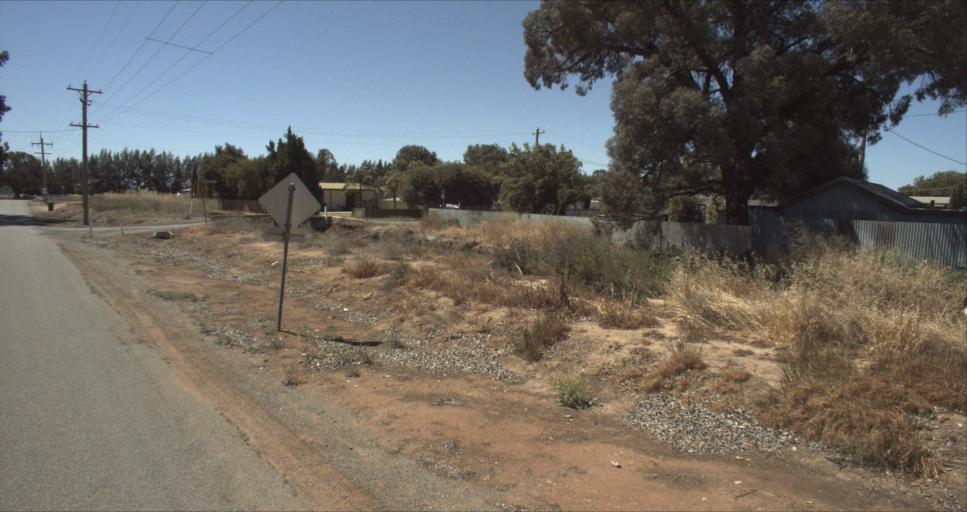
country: AU
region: New South Wales
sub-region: Leeton
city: Leeton
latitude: -34.5238
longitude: 146.3304
